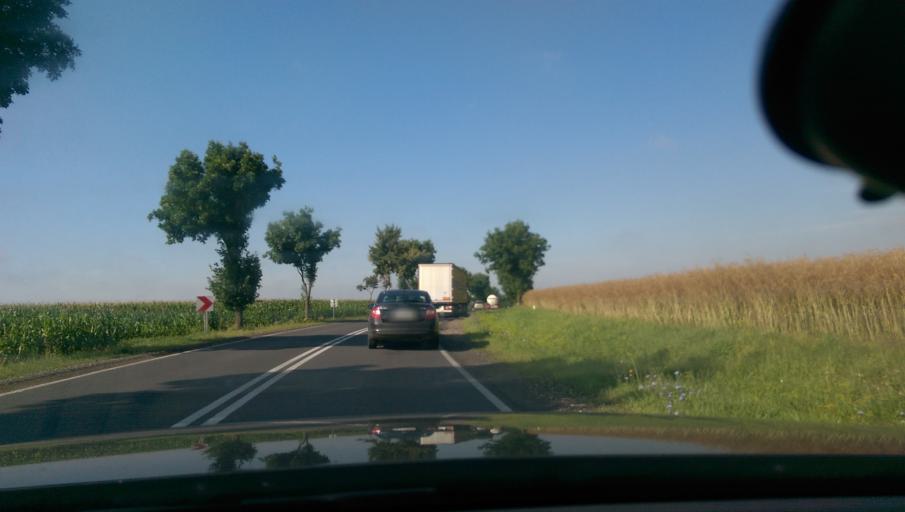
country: PL
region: Masovian Voivodeship
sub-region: Powiat plonski
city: Plonsk
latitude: 52.6395
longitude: 20.4028
